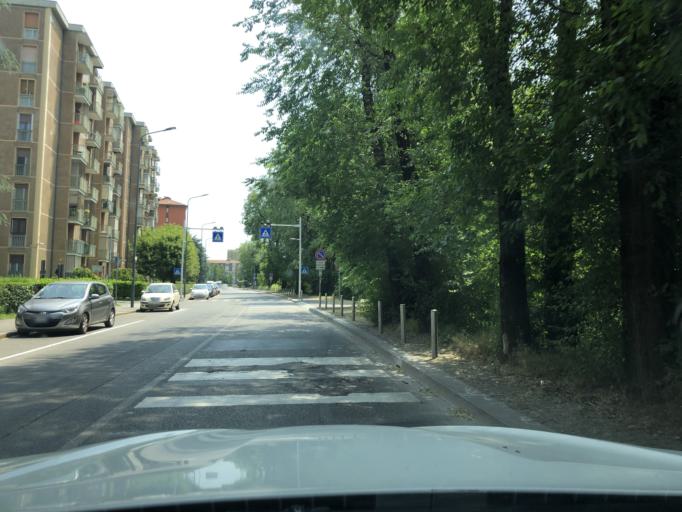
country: IT
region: Lombardy
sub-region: Citta metropolitana di Milano
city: Pero
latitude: 45.4964
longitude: 9.1017
